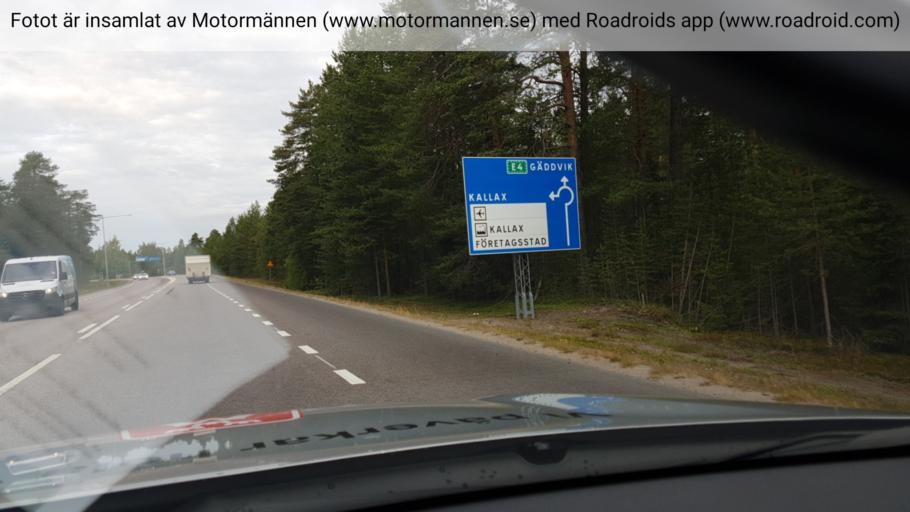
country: SE
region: Norrbotten
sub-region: Lulea Kommun
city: Bergnaset
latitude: 65.5788
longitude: 22.0822
